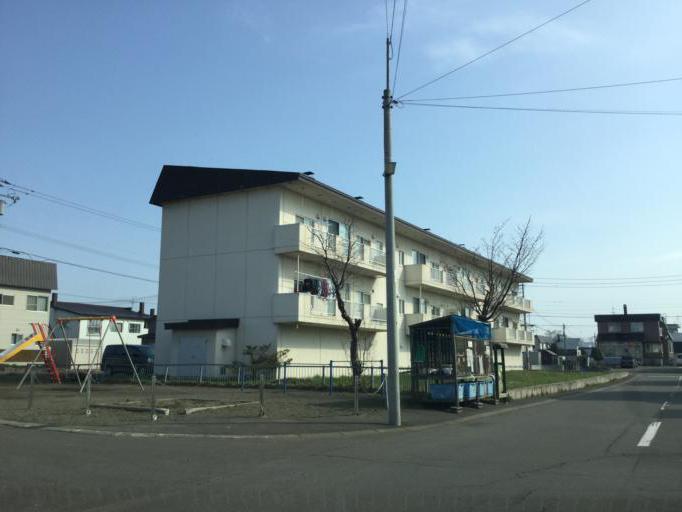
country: JP
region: Hokkaido
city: Iwamizawa
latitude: 43.2100
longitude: 141.7732
